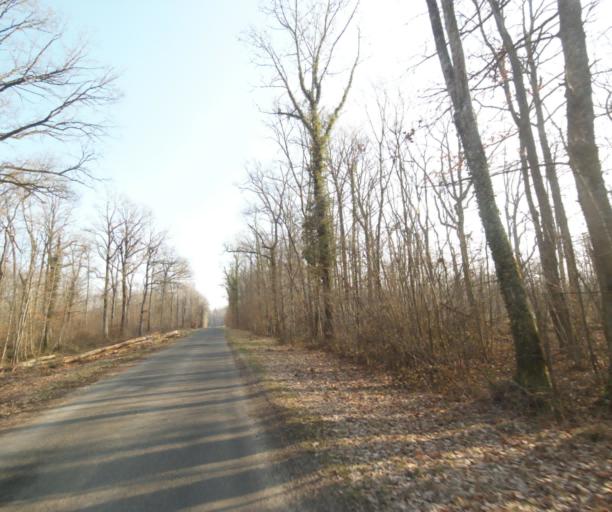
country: FR
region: Champagne-Ardenne
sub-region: Departement de la Haute-Marne
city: Wassy
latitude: 48.4583
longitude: 4.9283
